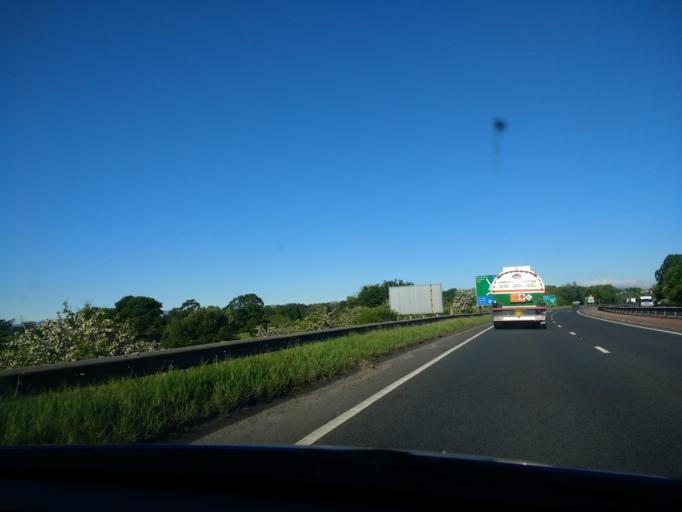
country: GB
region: England
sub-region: Cumbria
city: Penrith
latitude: 54.6505
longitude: -2.7547
